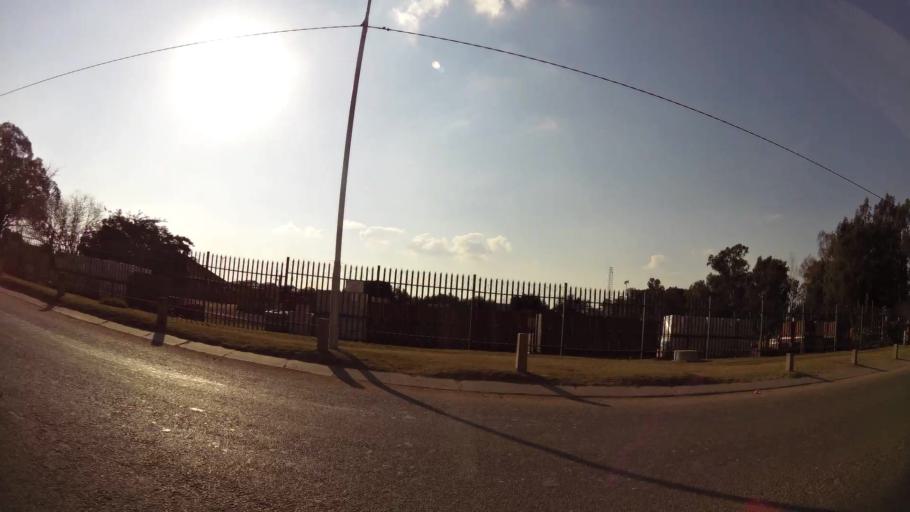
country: ZA
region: Gauteng
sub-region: Ekurhuleni Metropolitan Municipality
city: Tembisa
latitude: -25.9417
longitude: 28.2319
